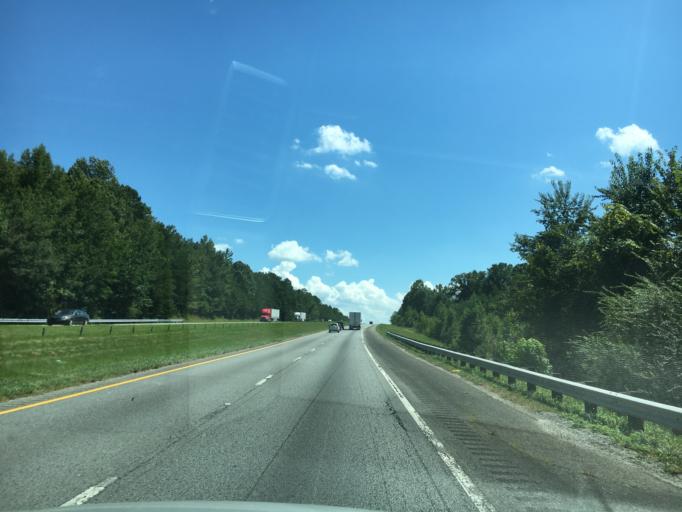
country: US
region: South Carolina
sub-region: Spartanburg County
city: Roebuck
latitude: 34.8198
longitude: -81.9637
